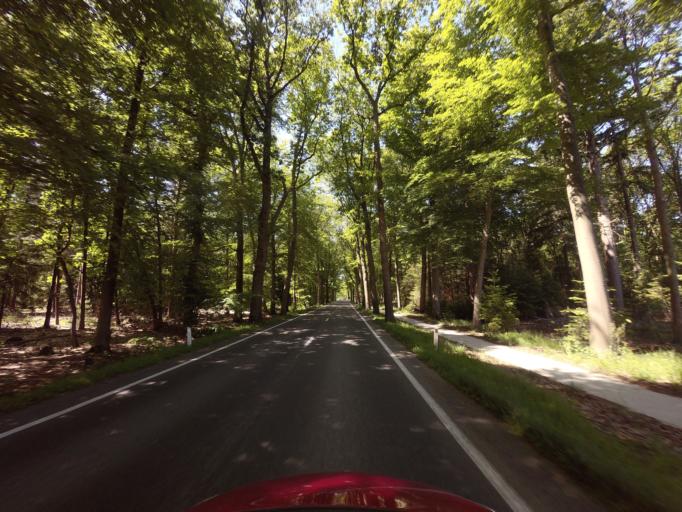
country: BE
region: Flanders
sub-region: Provincie Antwerpen
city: Ravels
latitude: 51.3753
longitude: 5.0408
